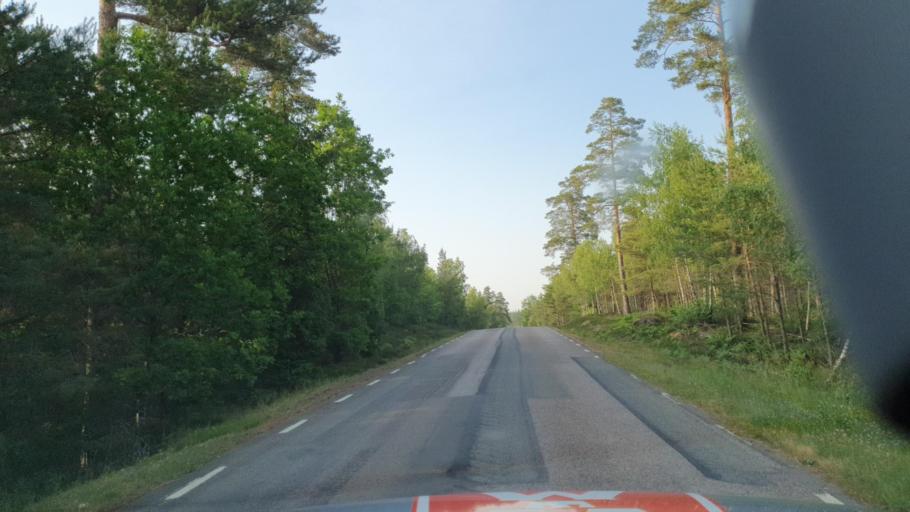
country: SE
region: Kalmar
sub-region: Torsas Kommun
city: Torsas
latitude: 56.4860
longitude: 16.0962
